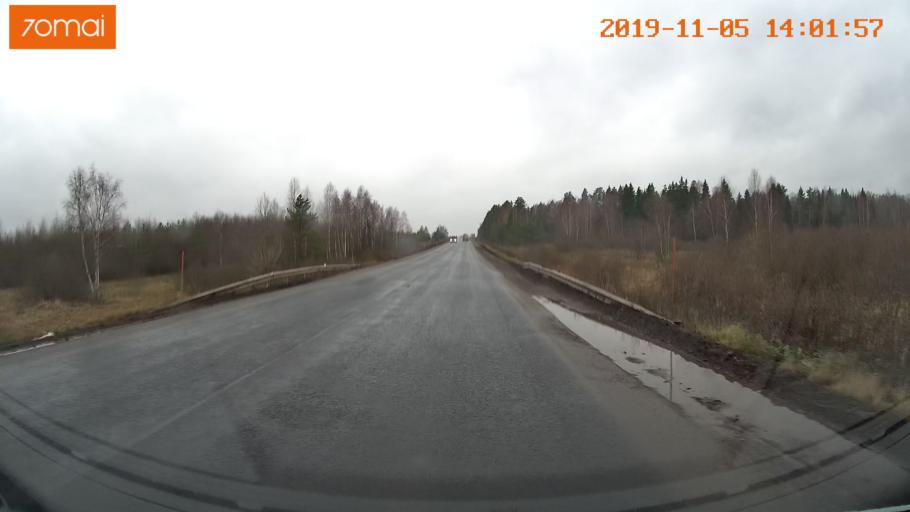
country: RU
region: Ivanovo
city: Kokhma
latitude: 57.0055
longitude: 41.2222
